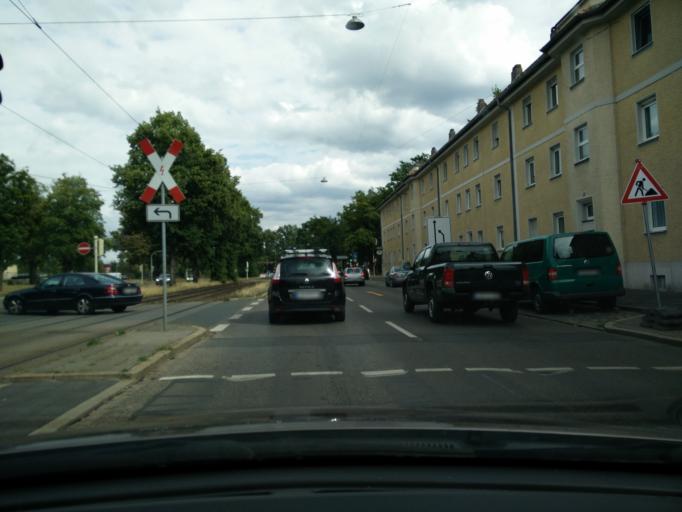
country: DE
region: Bavaria
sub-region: Regierungsbezirk Mittelfranken
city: Nuernberg
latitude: 49.4399
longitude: 11.1111
